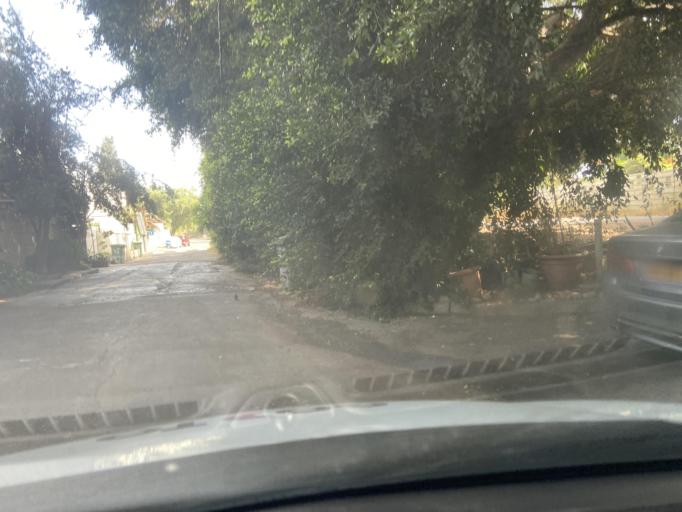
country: IL
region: Central District
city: Yehud
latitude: 32.0375
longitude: 34.8913
